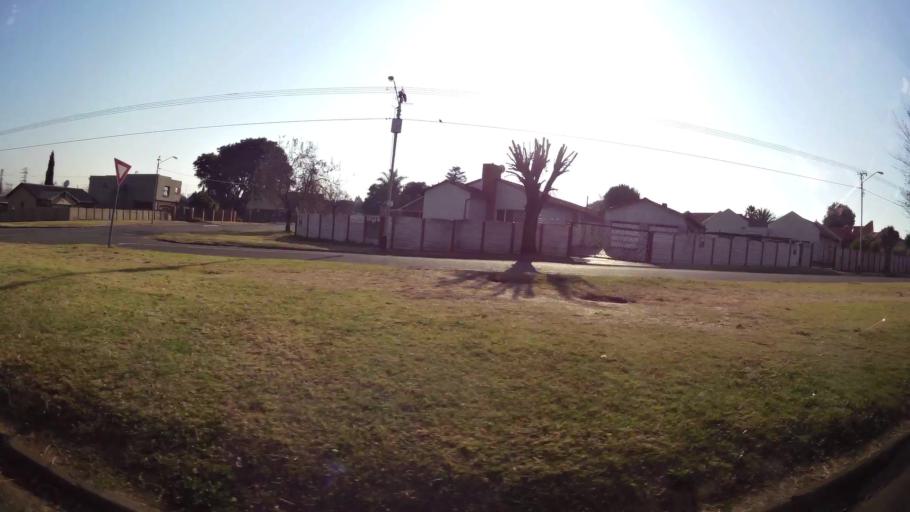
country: ZA
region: Gauteng
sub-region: City of Johannesburg Metropolitan Municipality
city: Modderfontein
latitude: -26.1459
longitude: 28.1959
